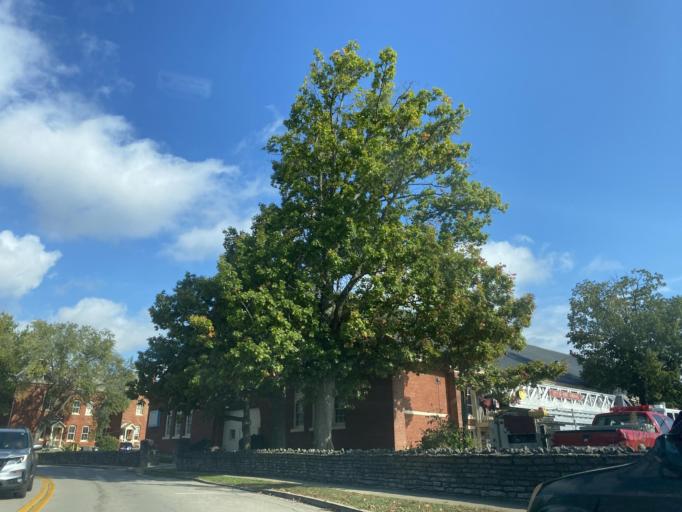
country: US
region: Kentucky
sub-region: Campbell County
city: Fort Thomas
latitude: 39.0656
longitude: -84.4461
